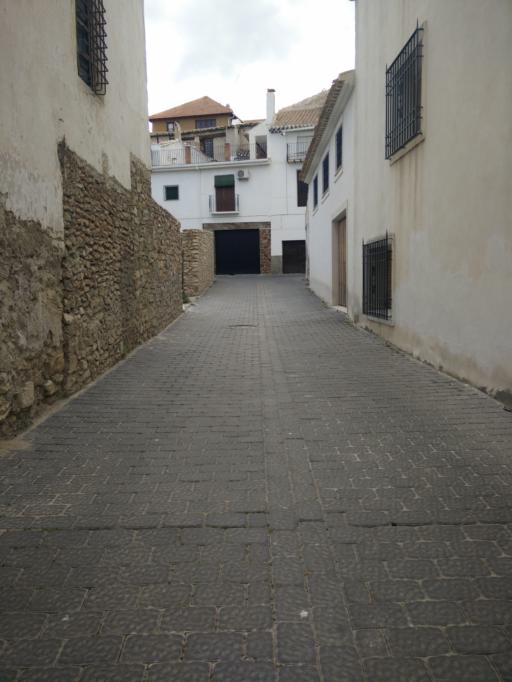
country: ES
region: Andalusia
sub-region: Provincia de Granada
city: Puebla de Don Fadrique
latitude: 37.9603
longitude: -2.4367
